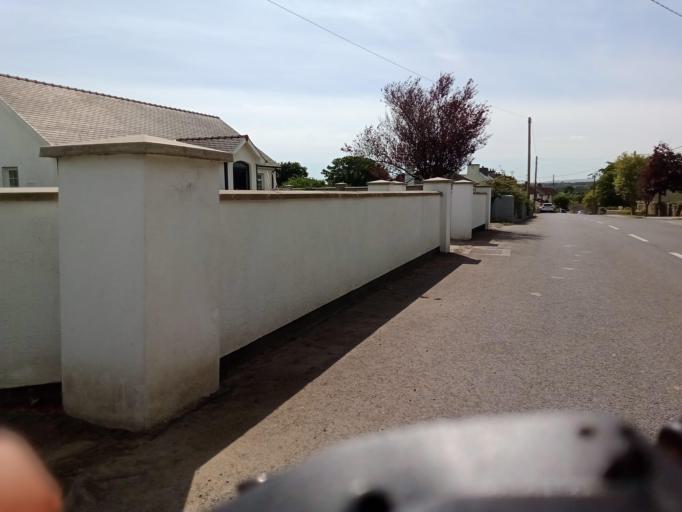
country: IE
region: Munster
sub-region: Waterford
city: Dungarvan
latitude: 52.1325
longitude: -7.4585
